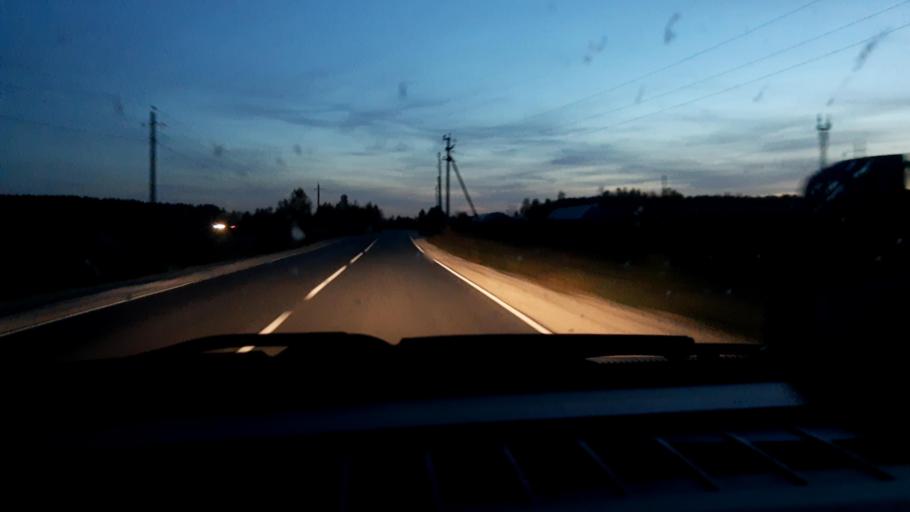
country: RU
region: Nizjnij Novgorod
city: Neklyudovo
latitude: 56.4522
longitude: 43.9026
